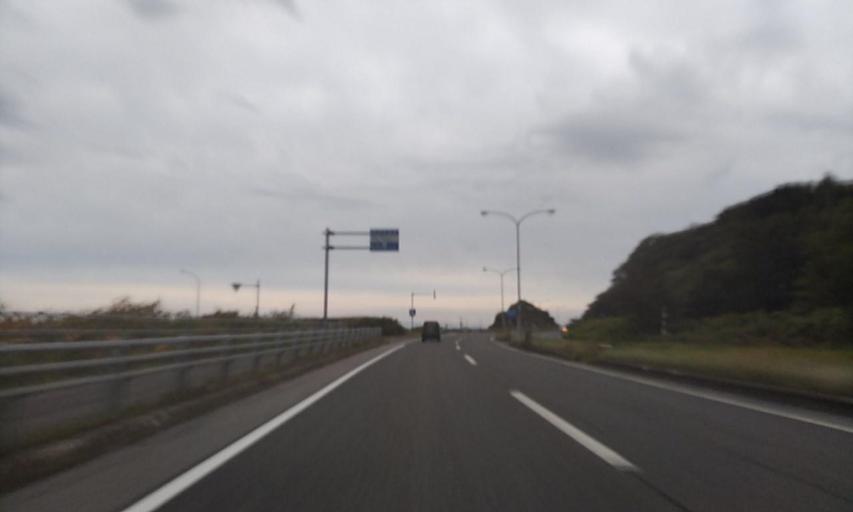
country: JP
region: Hokkaido
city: Abashiri
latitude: 43.9943
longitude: 144.2958
